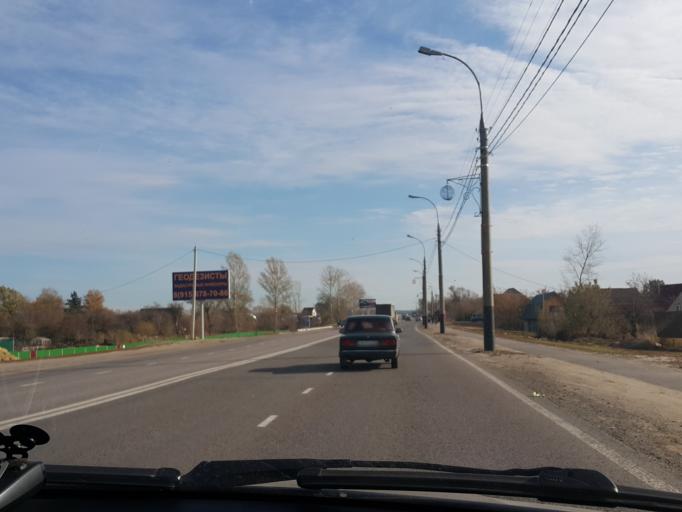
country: RU
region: Tambov
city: Tambov
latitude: 52.7235
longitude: 41.4740
